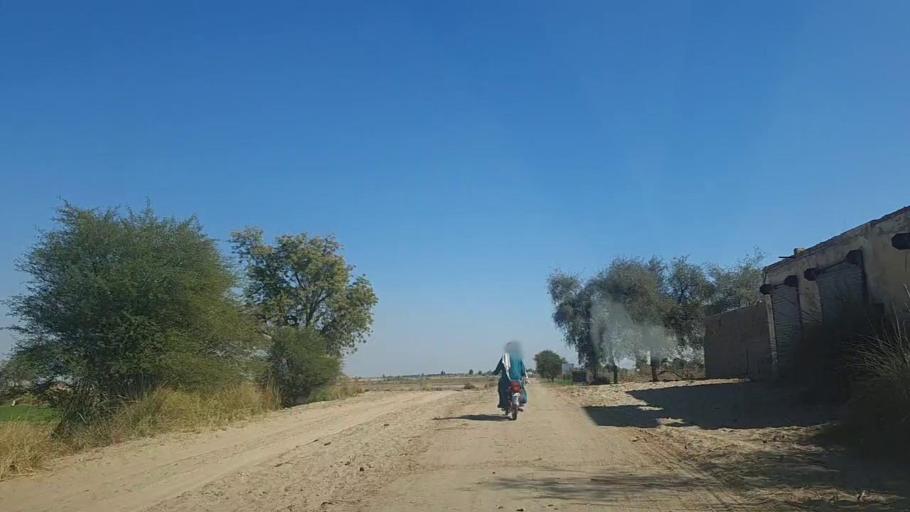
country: PK
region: Sindh
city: Sanghar
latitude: 26.2093
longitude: 68.8845
